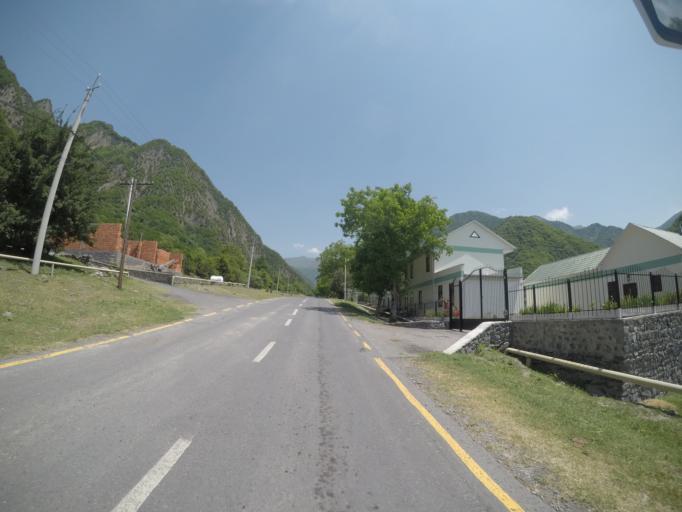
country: AZ
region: Qakh Rayon
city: Qaxbas
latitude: 41.4533
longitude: 47.0122
